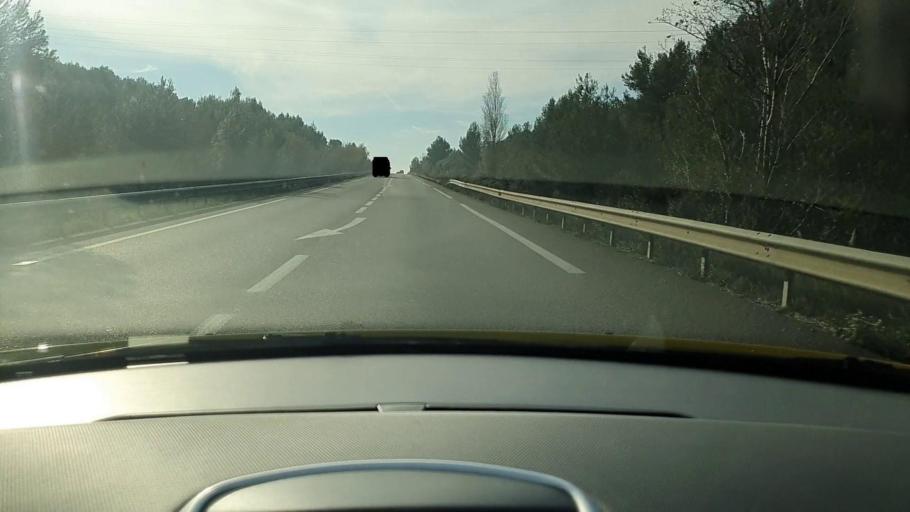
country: FR
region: Languedoc-Roussillon
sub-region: Departement du Gard
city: Comps
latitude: 43.8275
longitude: 4.6142
